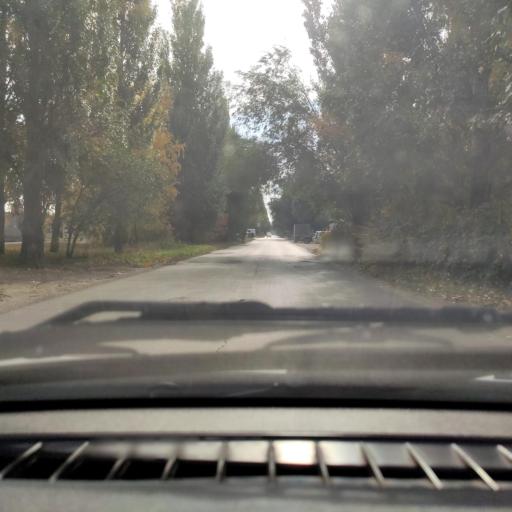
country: RU
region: Samara
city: Tol'yatti
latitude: 53.5376
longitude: 49.4166
